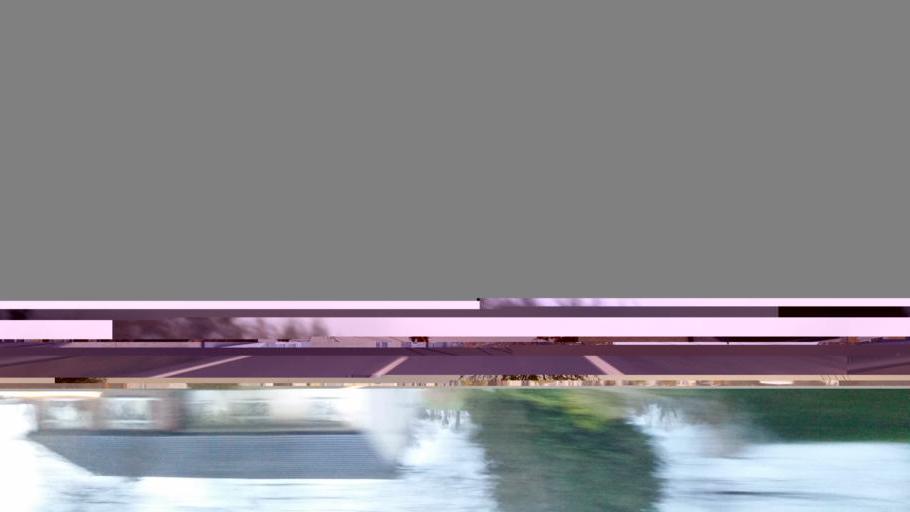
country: IE
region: Ulster
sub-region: County Monaghan
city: Monaghan
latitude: 54.4330
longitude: -6.9917
